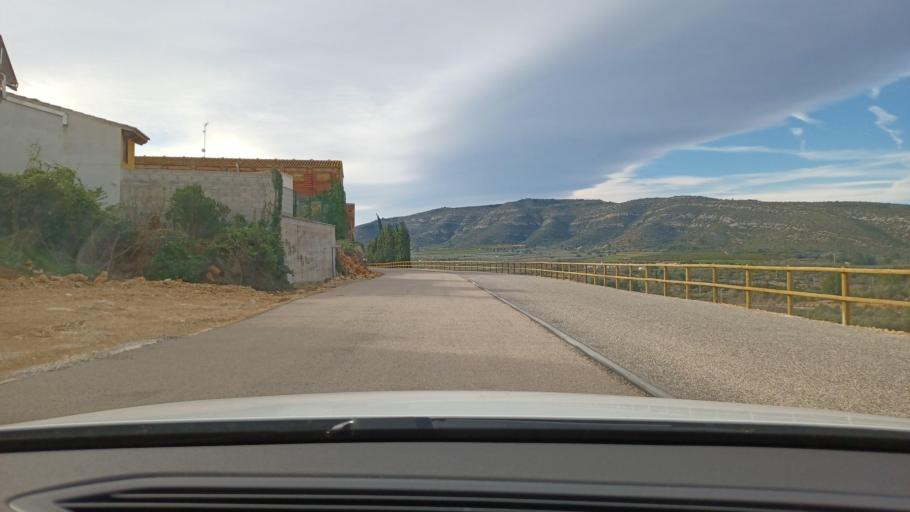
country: ES
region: Catalonia
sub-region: Provincia de Tarragona
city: Masdenverge
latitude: 40.6728
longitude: 0.5196
